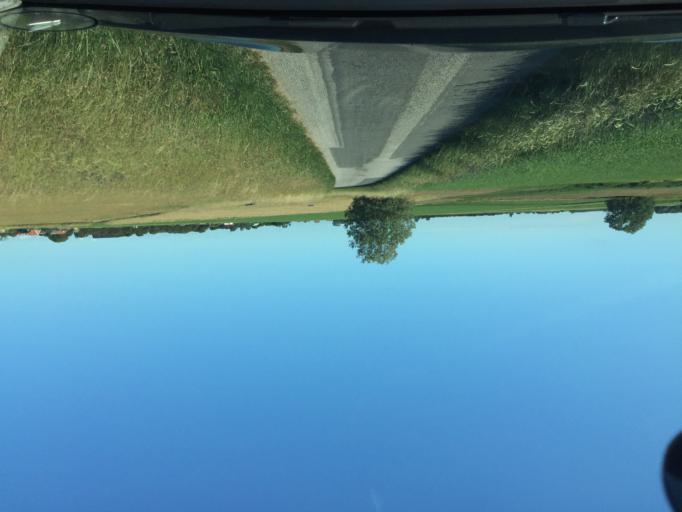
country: DK
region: Zealand
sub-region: Slagelse Kommune
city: Skaelskor
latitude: 55.2055
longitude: 11.1822
